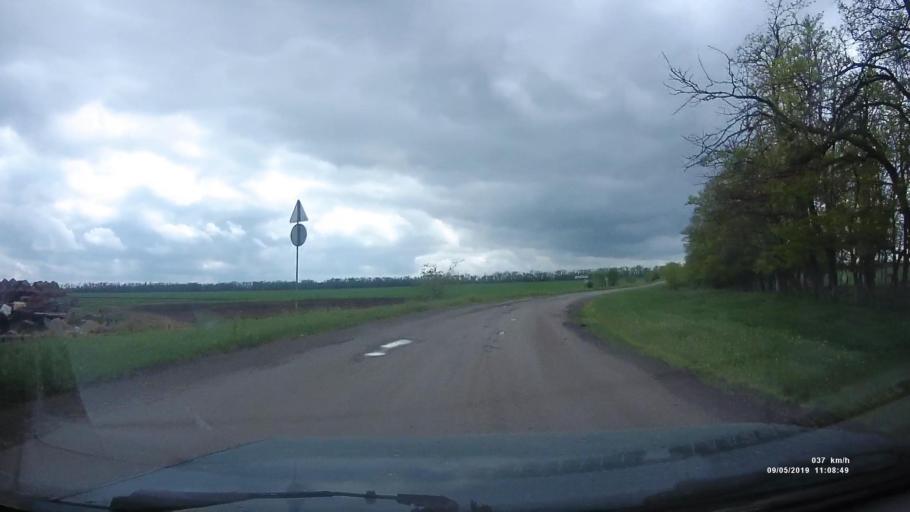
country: RU
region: Krasnodarskiy
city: Kanelovskaya
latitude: 46.7876
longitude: 39.2117
